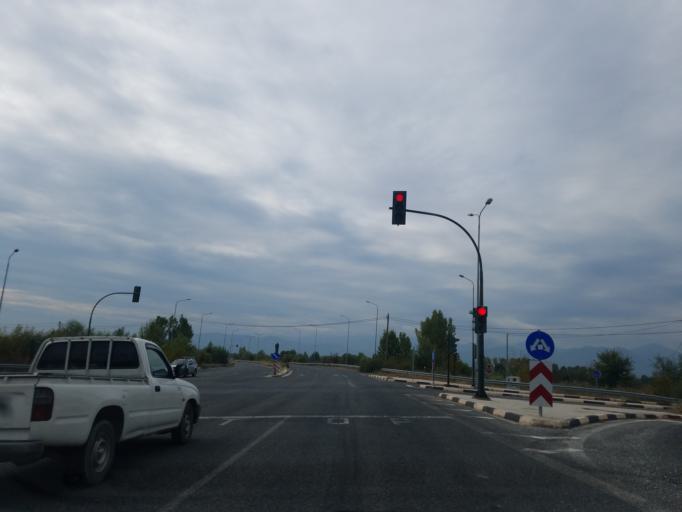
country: GR
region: Thessaly
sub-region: Trikala
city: Pyrgetos
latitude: 39.5583
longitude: 21.7340
